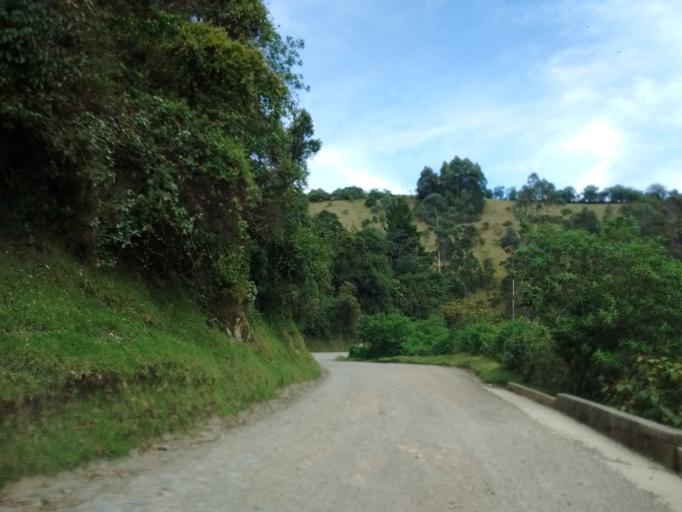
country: CO
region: Cauca
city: Totoro
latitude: 2.3819
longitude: -76.4502
